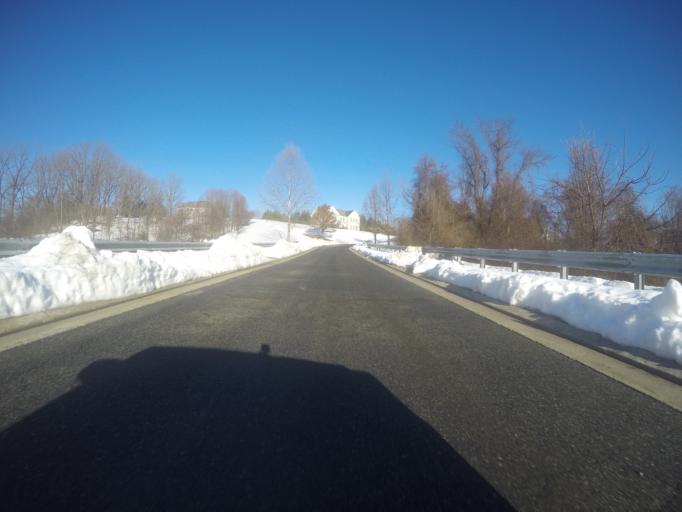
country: US
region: Maryland
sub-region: Baltimore County
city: Hunt Valley
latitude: 39.5291
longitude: -76.6395
